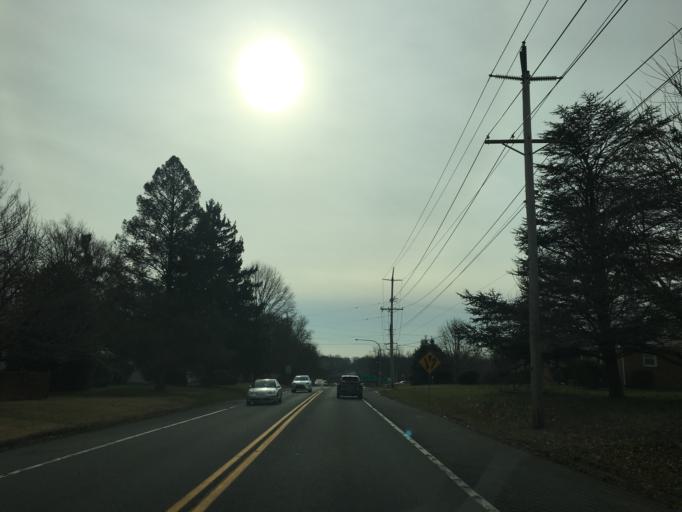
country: US
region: Delaware
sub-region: New Castle County
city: Bellefonte
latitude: 39.7837
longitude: -75.5061
